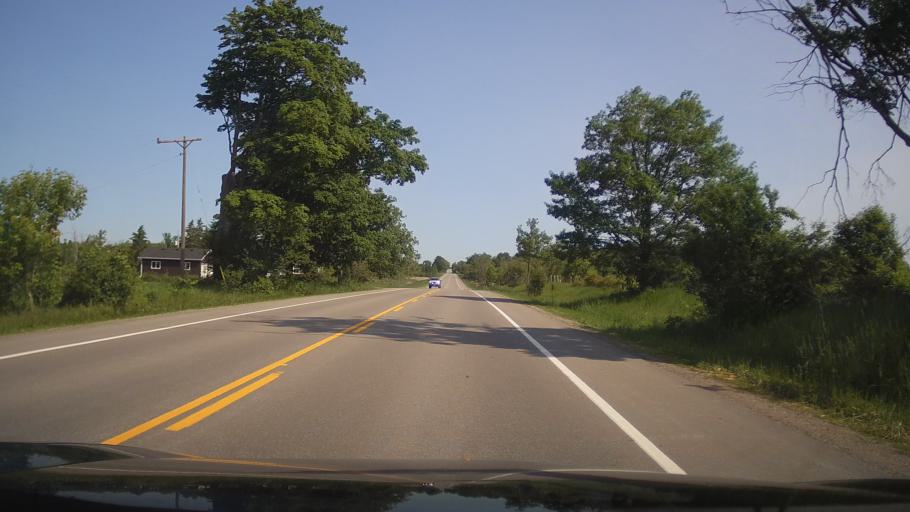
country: CA
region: Ontario
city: Omemee
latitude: 44.3498
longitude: -78.8872
